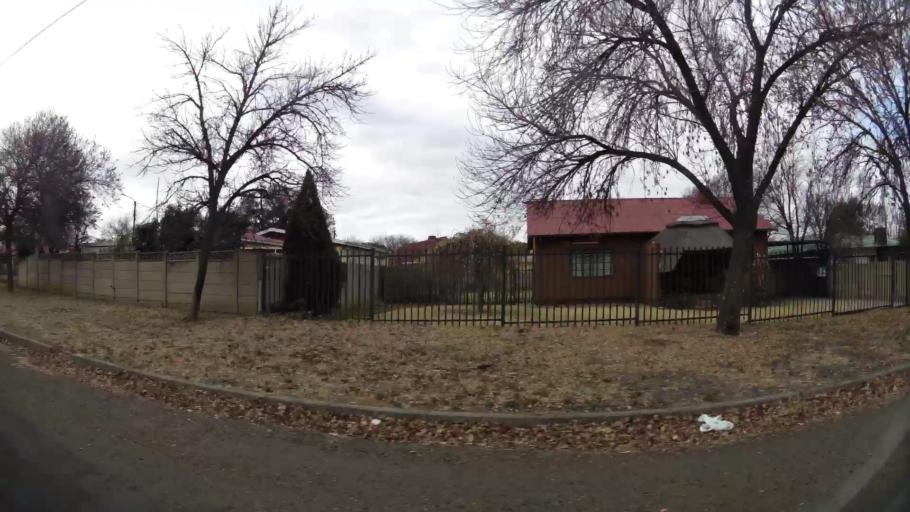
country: ZA
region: Orange Free State
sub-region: Fezile Dabi District Municipality
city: Kroonstad
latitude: -27.6342
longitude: 27.2280
